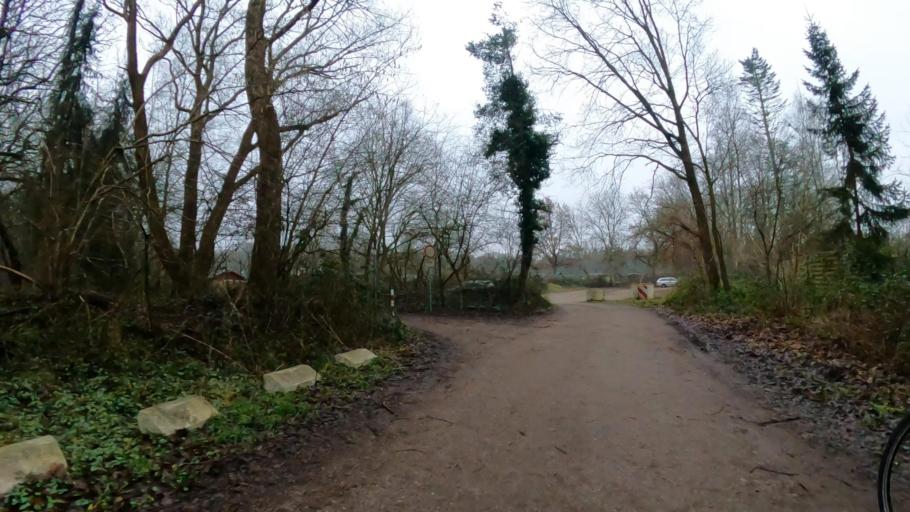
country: DE
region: Schleswig-Holstein
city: Wedel
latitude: 53.5968
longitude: 9.7333
